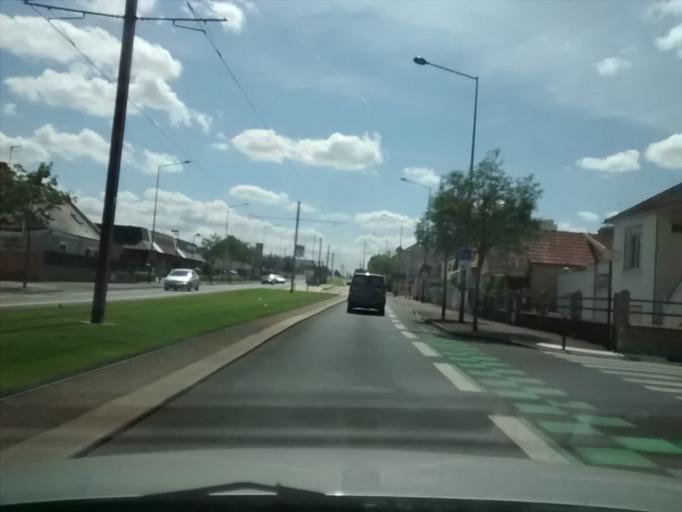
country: FR
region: Pays de la Loire
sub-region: Departement de la Sarthe
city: Le Mans
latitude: 47.9760
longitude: 0.2145
